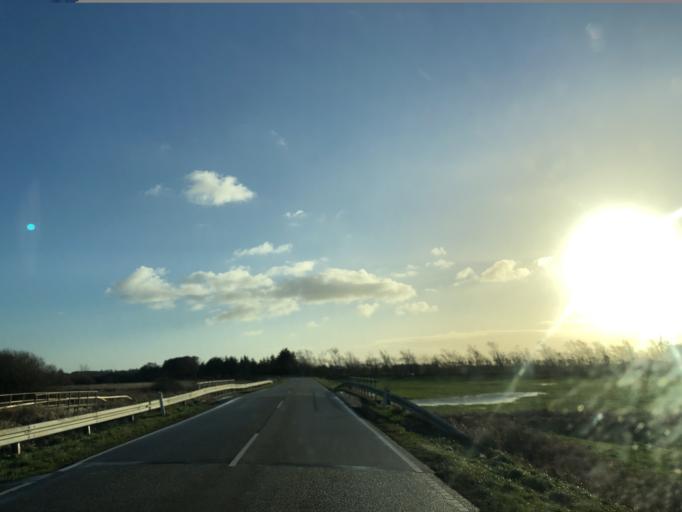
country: DK
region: Central Jutland
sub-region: Holstebro Kommune
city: Ulfborg
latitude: 56.2022
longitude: 8.2638
